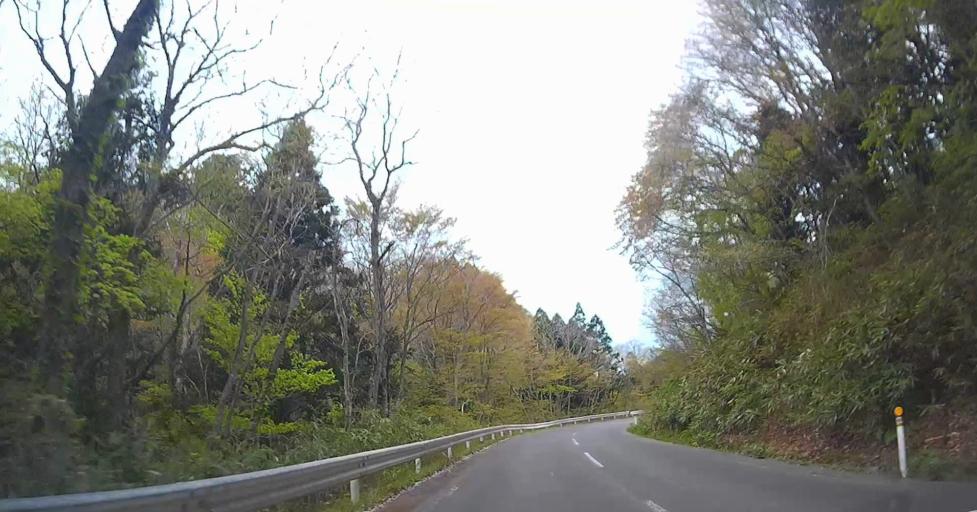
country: JP
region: Aomori
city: Goshogawara
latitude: 40.9044
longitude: 140.5211
